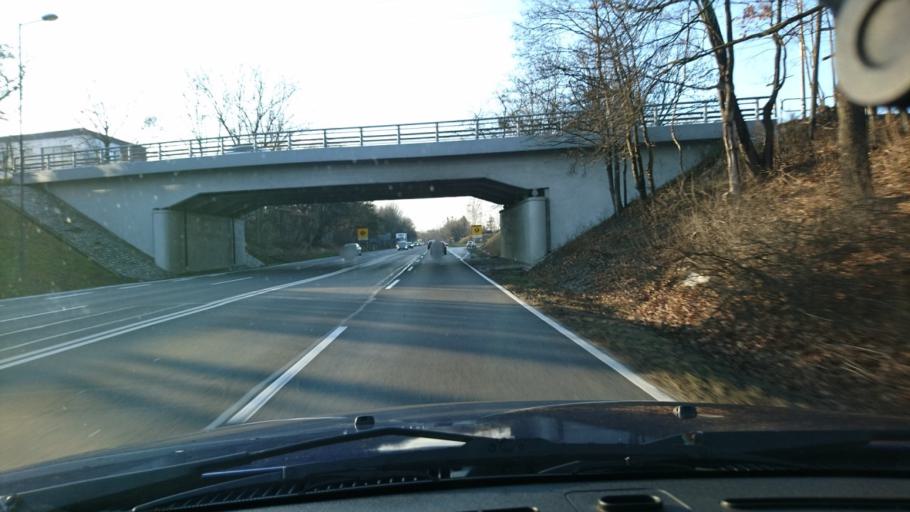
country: PL
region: Silesian Voivodeship
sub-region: Gliwice
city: Gliwice
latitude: 50.3150
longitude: 18.6940
